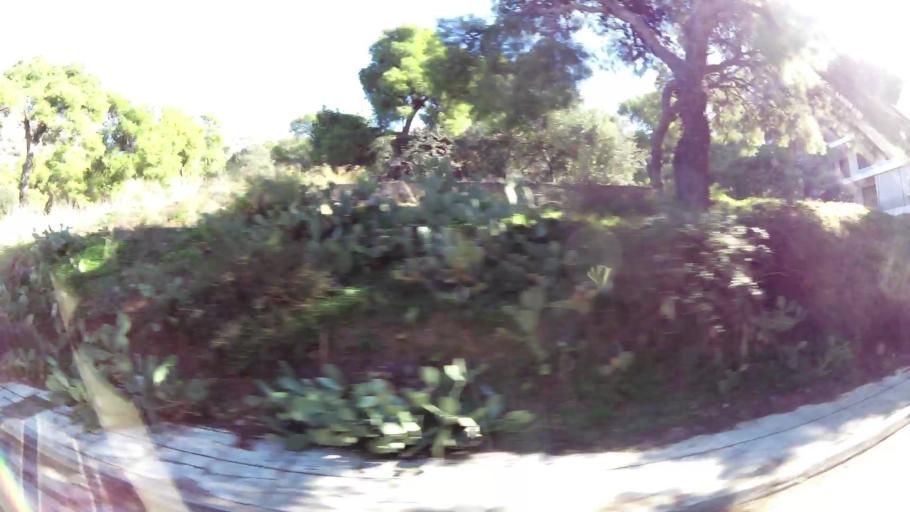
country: GR
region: Attica
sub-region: Nomarchia Anatolikis Attikis
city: Vouliagmeni
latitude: 37.8154
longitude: 23.7879
